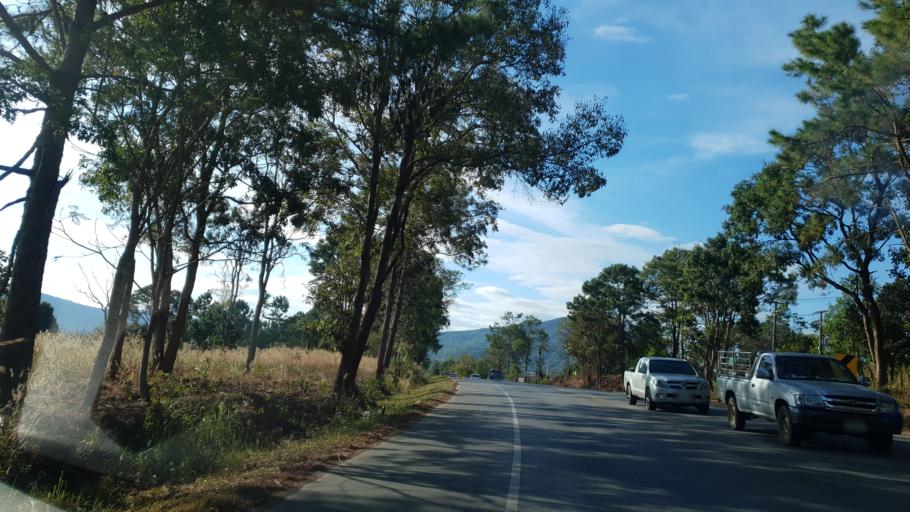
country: TH
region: Loei
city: Phu Ruea
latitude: 17.4506
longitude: 101.4847
